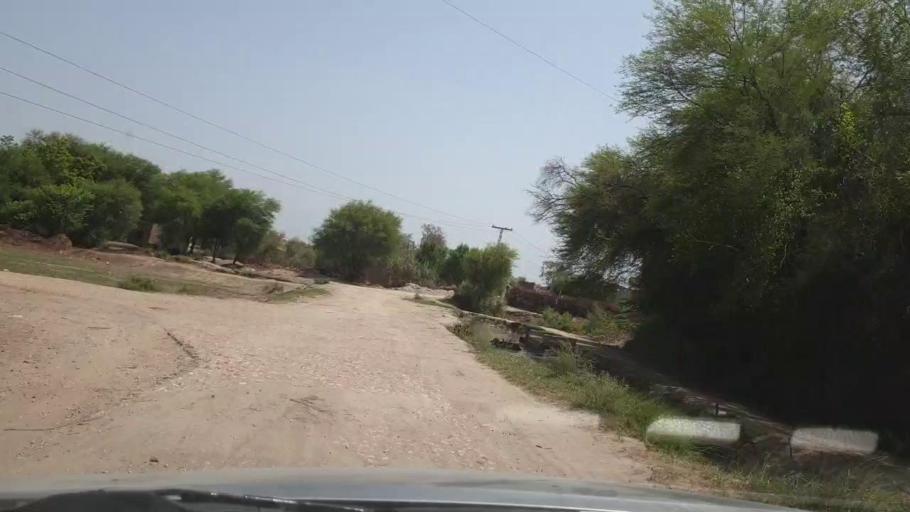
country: PK
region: Sindh
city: Pano Aqil
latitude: 27.8160
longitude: 69.2306
